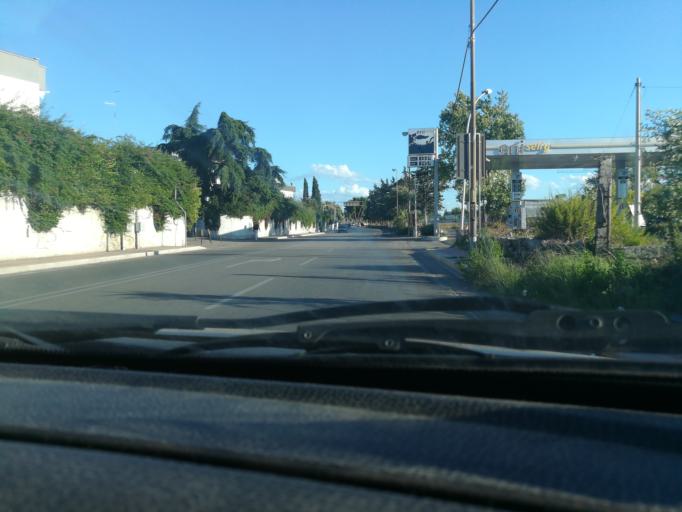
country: IT
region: Apulia
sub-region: Provincia di Bari
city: Bari
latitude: 41.0879
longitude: 16.8845
